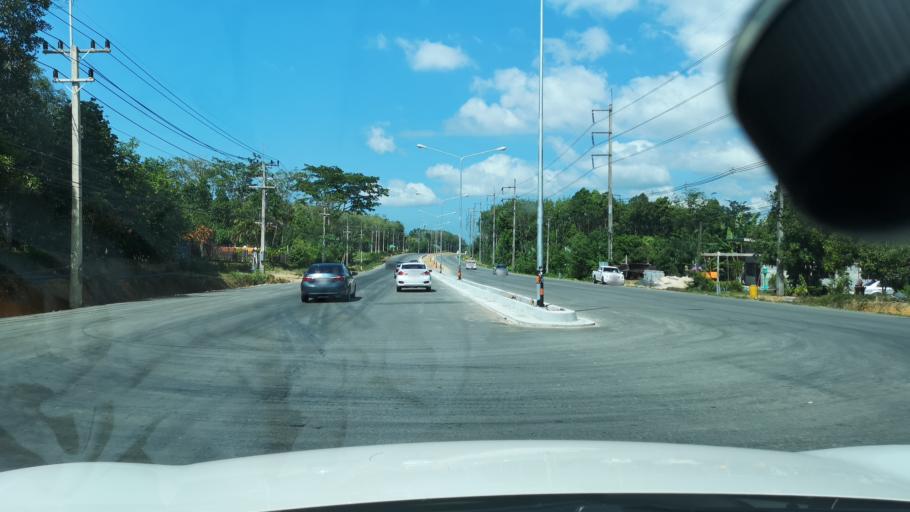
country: TH
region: Phangnga
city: Thai Mueang
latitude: 8.4340
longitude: 98.2575
